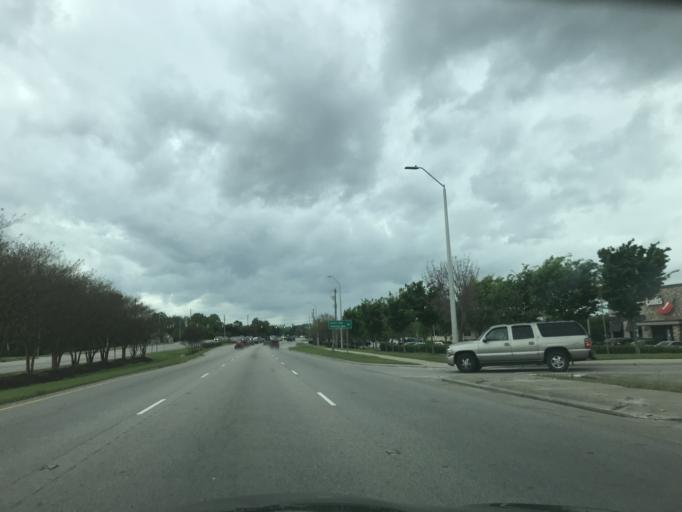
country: US
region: North Carolina
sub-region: Wake County
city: Knightdale
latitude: 35.7965
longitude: -78.5077
